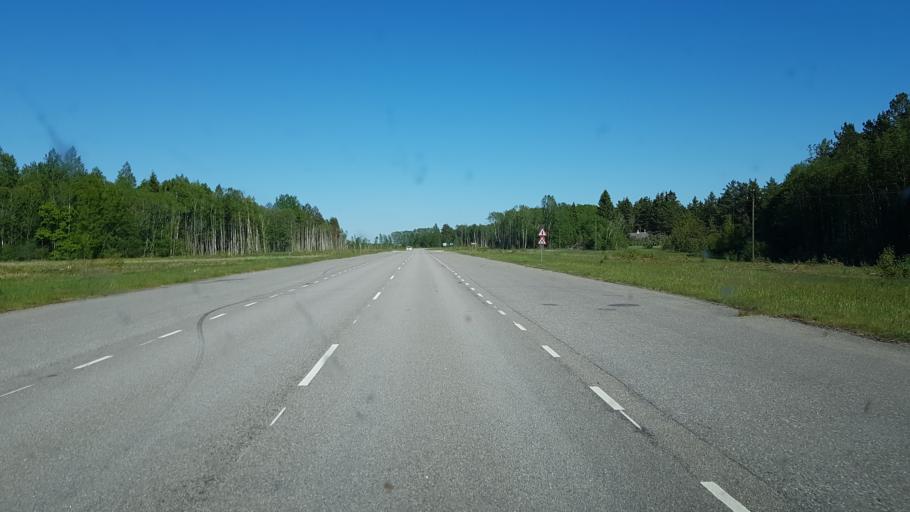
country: EE
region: Laeaene
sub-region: Lihula vald
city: Lihula
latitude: 58.5648
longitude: 23.8162
